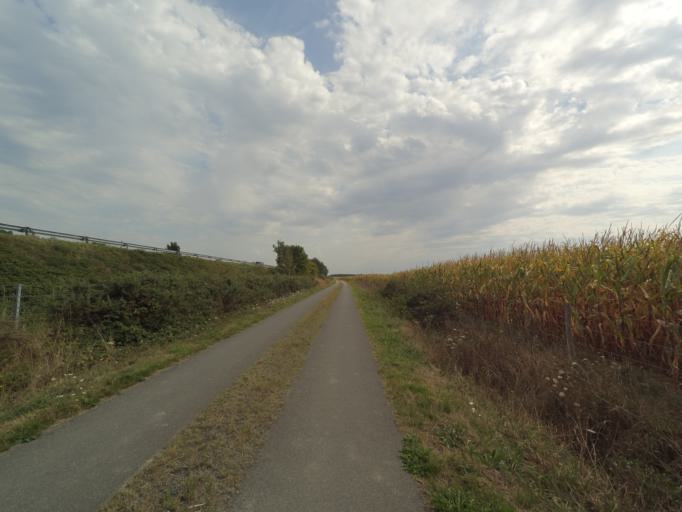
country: FR
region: Pays de la Loire
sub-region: Departement de la Vendee
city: Bouffere
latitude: 46.9869
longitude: -1.3804
